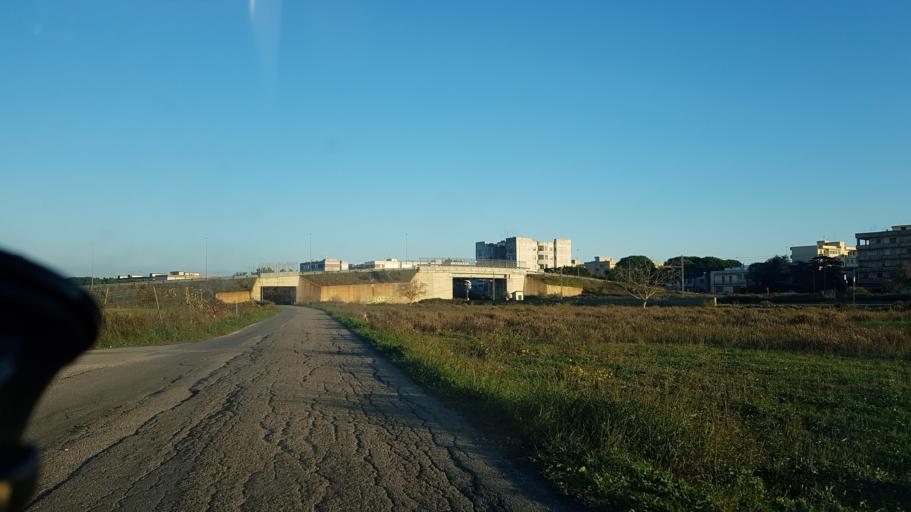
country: IT
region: Apulia
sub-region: Provincia di Brindisi
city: Mesagne
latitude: 40.5610
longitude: 17.7925
